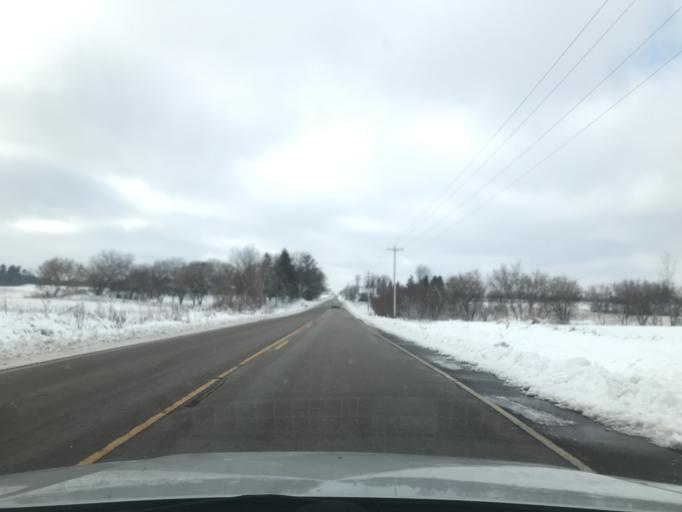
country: US
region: Wisconsin
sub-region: Oconto County
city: Oconto
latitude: 44.9499
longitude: -87.8899
